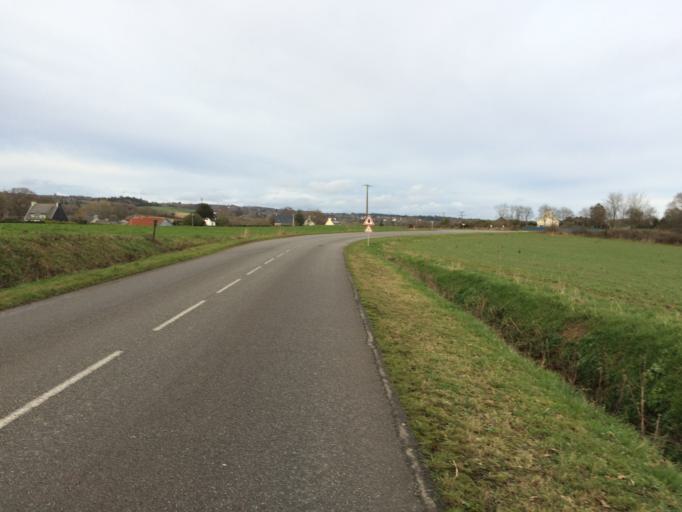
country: FR
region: Brittany
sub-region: Departement du Finistere
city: Daoulas
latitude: 48.3797
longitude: -4.2468
